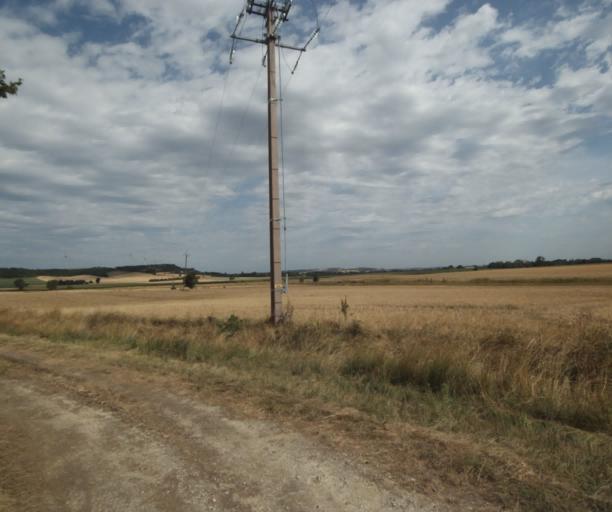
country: FR
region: Midi-Pyrenees
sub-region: Departement de la Haute-Garonne
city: Saint-Felix-Lauragais
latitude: 43.4482
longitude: 1.9308
